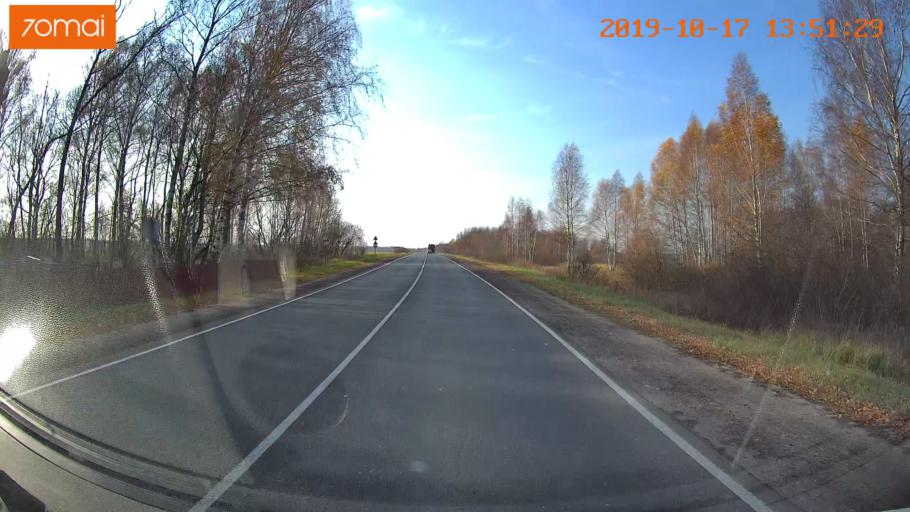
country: RU
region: Rjazan
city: Tuma
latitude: 55.1399
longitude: 40.3872
